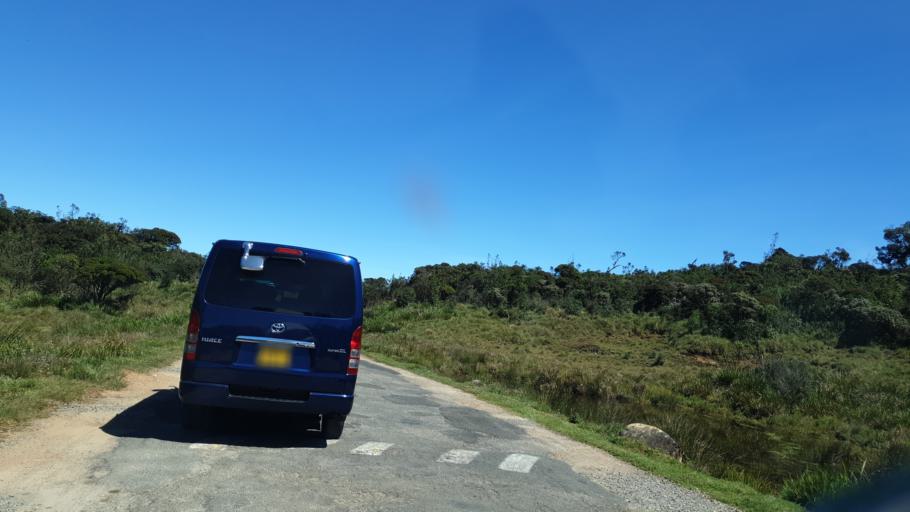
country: LK
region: Central
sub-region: Nuwara Eliya District
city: Nuwara Eliya
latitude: 6.8395
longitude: 80.8124
